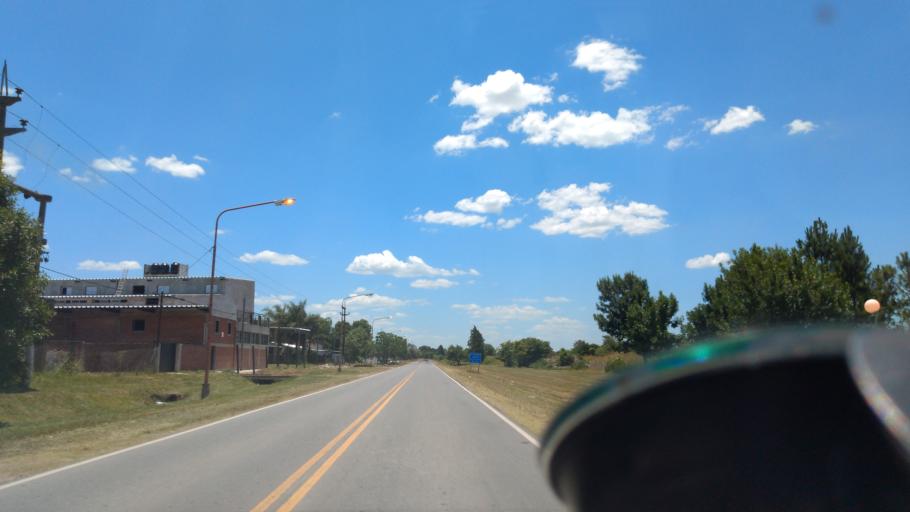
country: AR
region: Santa Fe
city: Laguna Paiva
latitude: -31.3206
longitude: -60.6588
